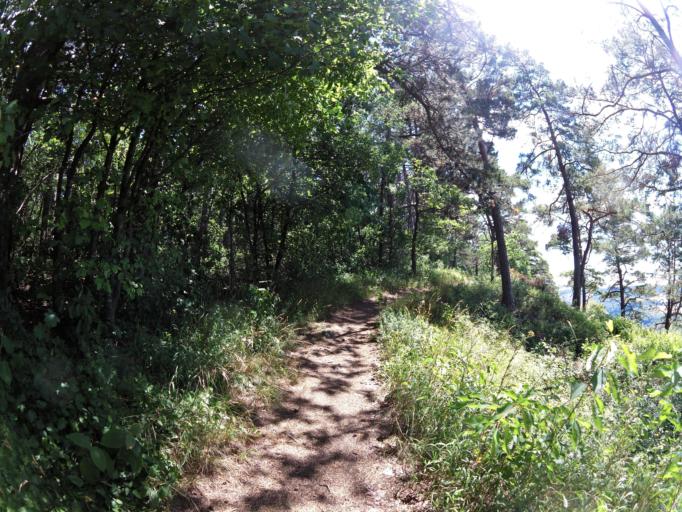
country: DE
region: Bavaria
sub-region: Regierungsbezirk Unterfranken
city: Zellingen
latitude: 49.8964
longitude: 9.8384
